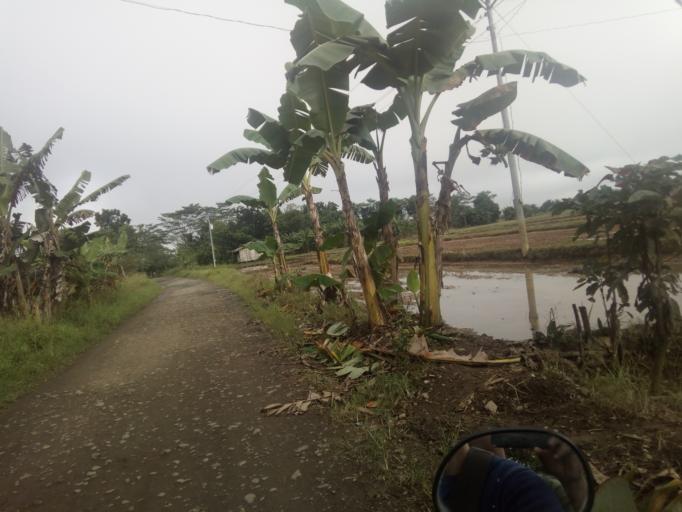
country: PH
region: Caraga
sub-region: Province of Agusan del Sur
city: Santa Josefa
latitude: 8.0234
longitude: 125.9927
